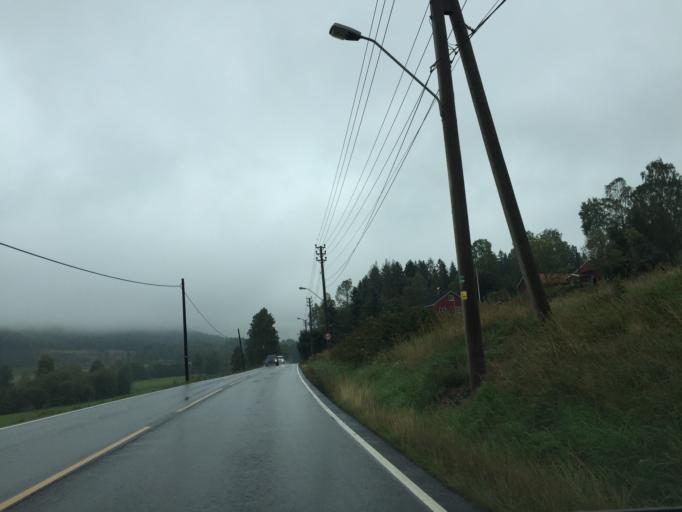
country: NO
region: Akershus
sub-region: Baerum
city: Lysaker
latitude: 59.9799
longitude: 10.6214
